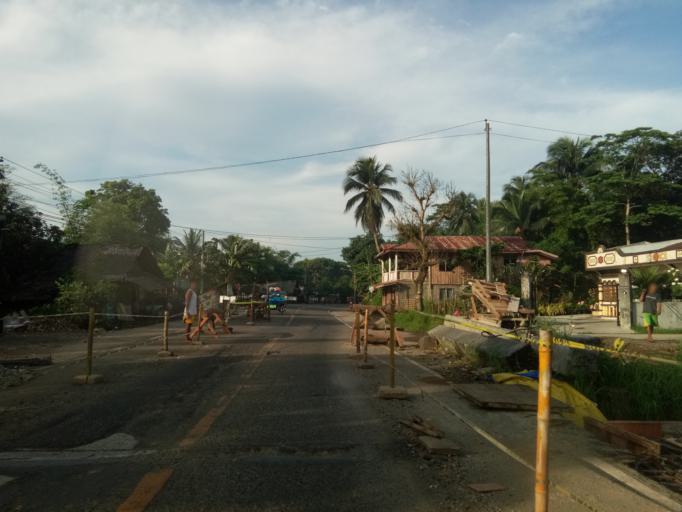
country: PH
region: Caraga
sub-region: Province of Surigao del Norte
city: Tubod
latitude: 9.5420
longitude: 125.5658
